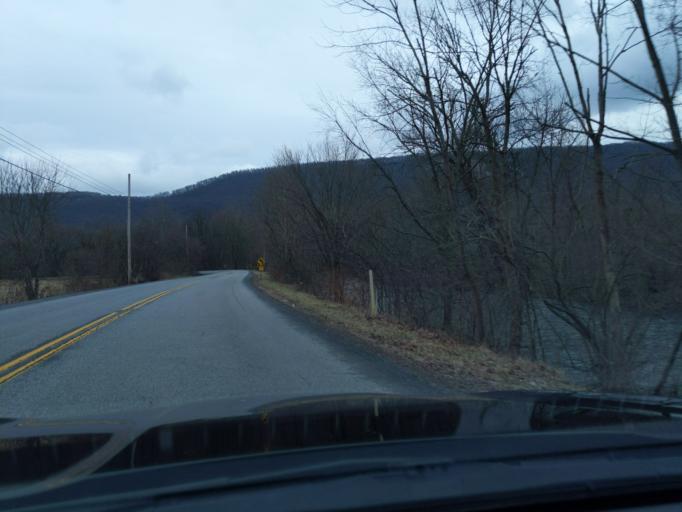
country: US
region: Pennsylvania
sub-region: Blair County
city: Tipton
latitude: 40.6272
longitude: -78.3012
